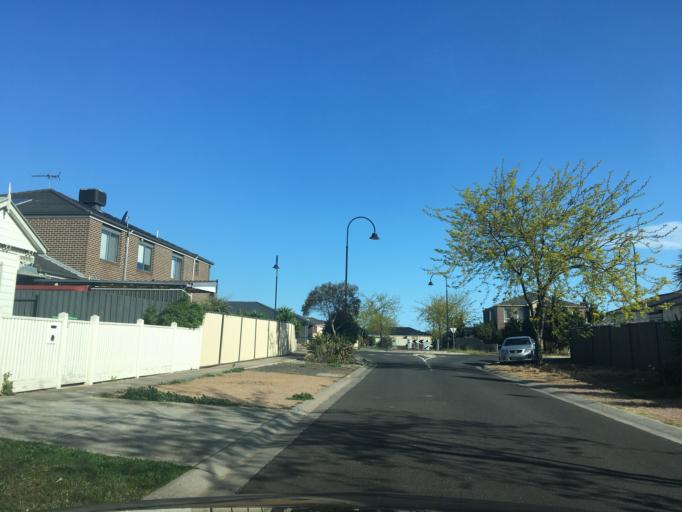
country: AU
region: Victoria
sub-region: Wyndham
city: Williams Landing
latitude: -37.8786
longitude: 144.7312
